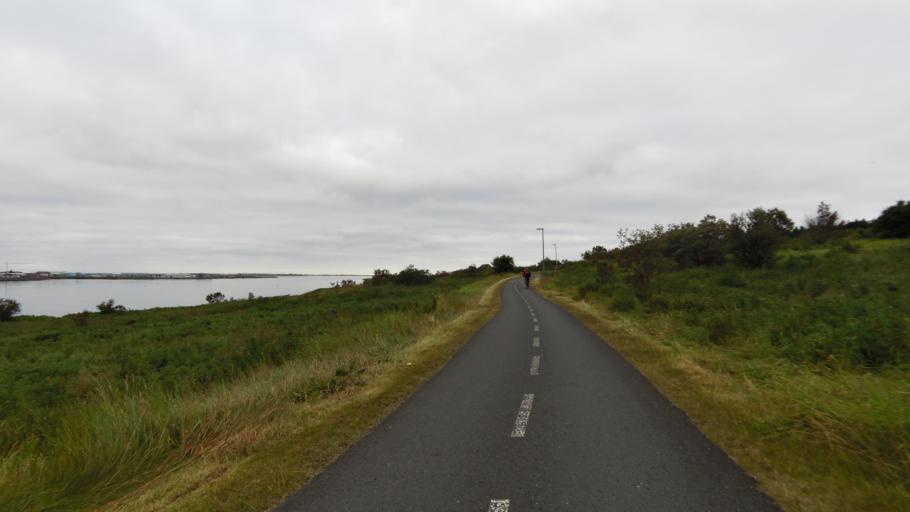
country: IS
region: Capital Region
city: Kopavogur
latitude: 64.1213
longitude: -21.9166
